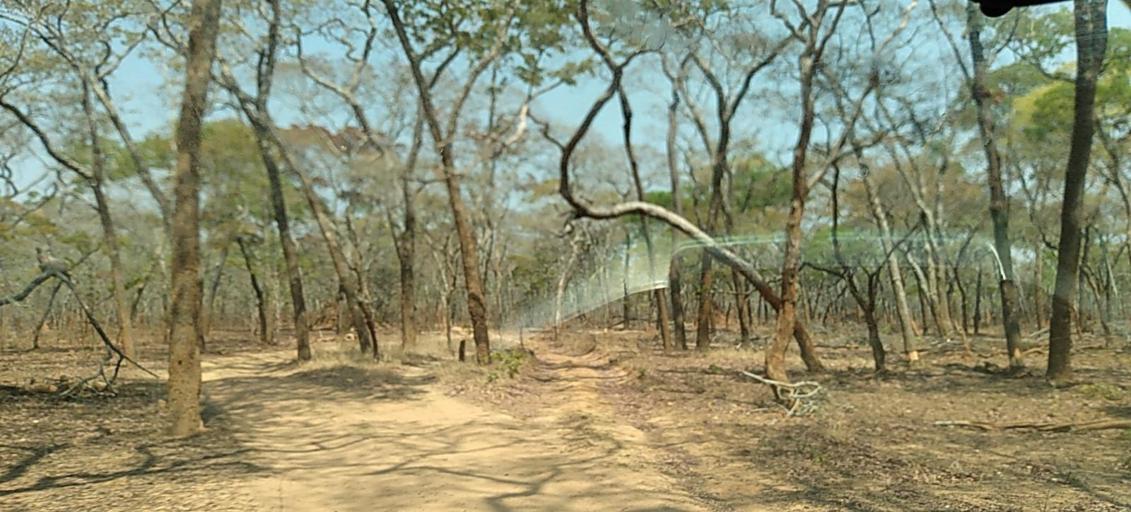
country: ZM
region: North-Western
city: Kasempa
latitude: -13.3926
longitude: 25.6065
